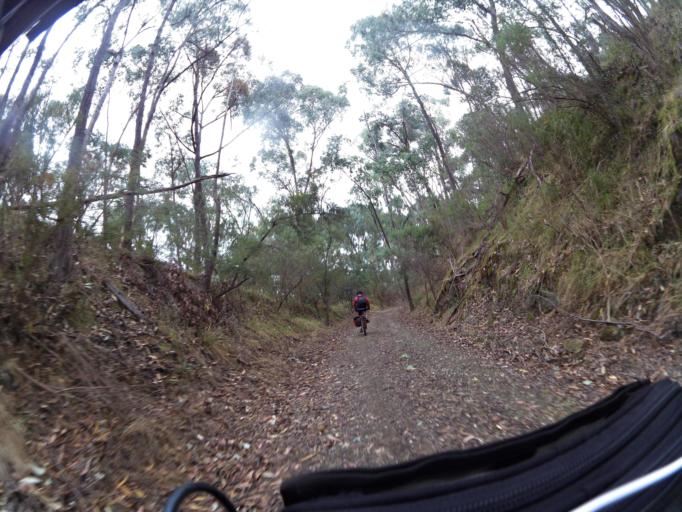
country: AU
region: New South Wales
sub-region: Greater Hume Shire
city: Holbrook
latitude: -36.1695
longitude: 147.4064
